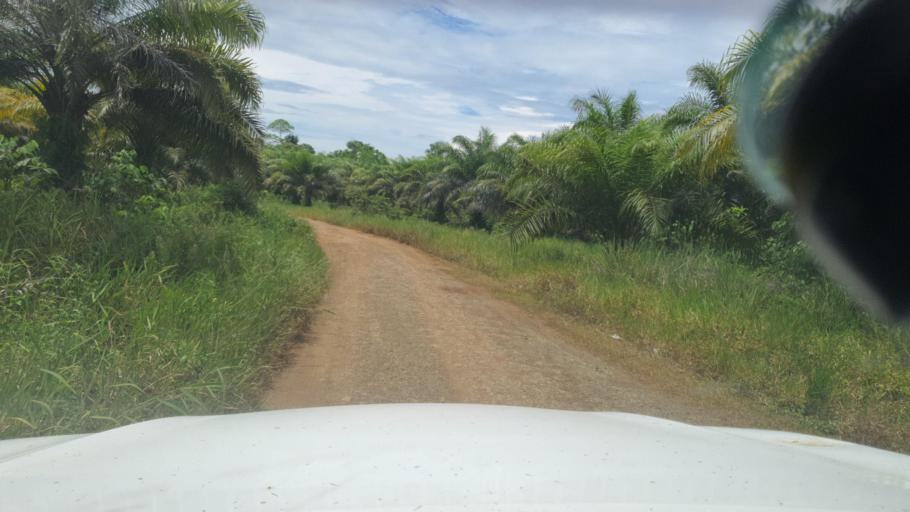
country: SB
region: Guadalcanal
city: Honiara
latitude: -9.4853
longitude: 160.3280
